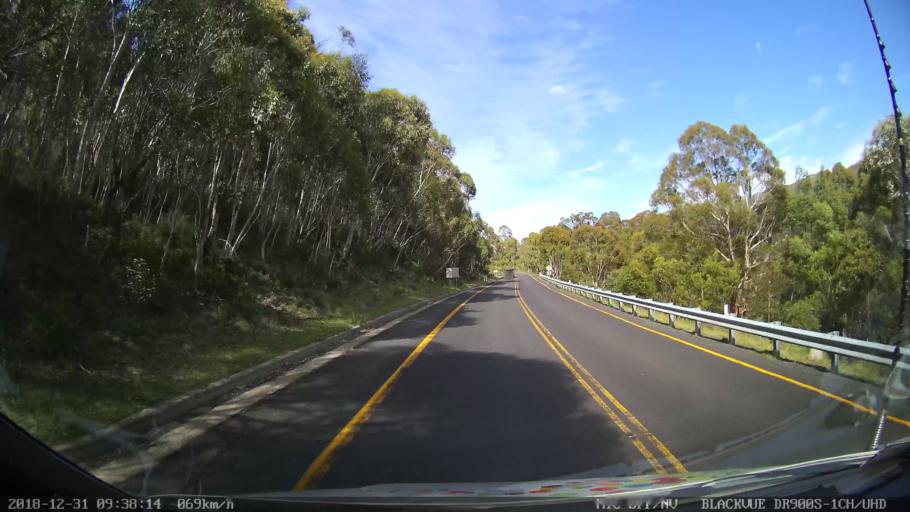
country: AU
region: New South Wales
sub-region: Snowy River
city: Jindabyne
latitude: -36.4731
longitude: 148.3698
